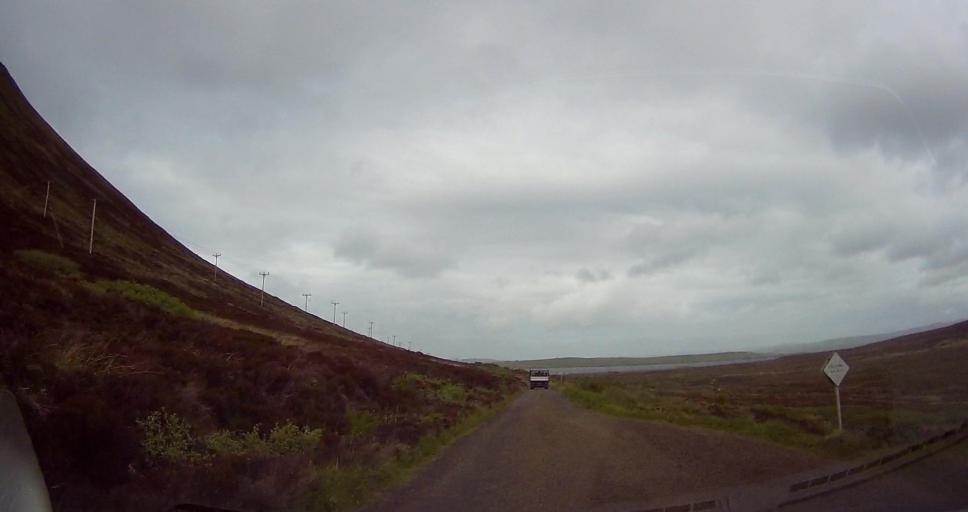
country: GB
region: Scotland
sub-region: Orkney Islands
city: Stromness
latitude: 58.8912
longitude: -3.3150
